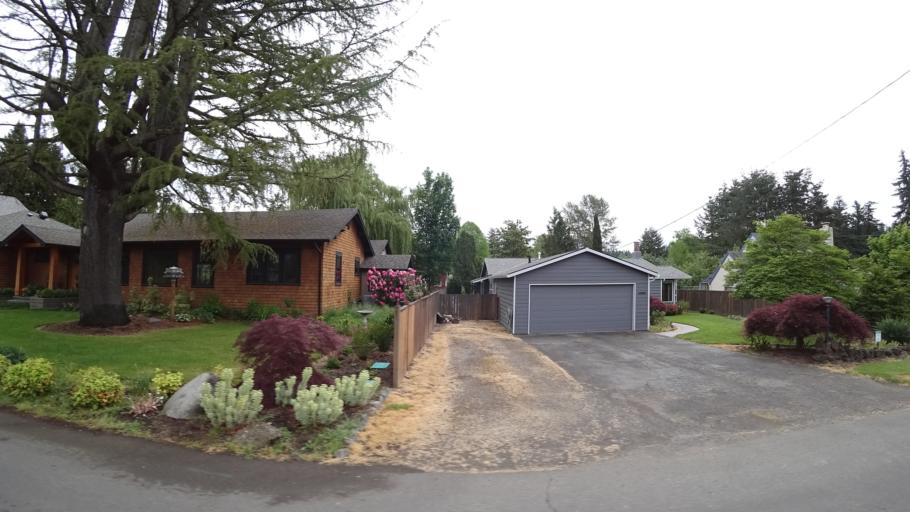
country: US
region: Oregon
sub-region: Washington County
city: Garden Home-Whitford
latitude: 45.4636
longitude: -122.7462
